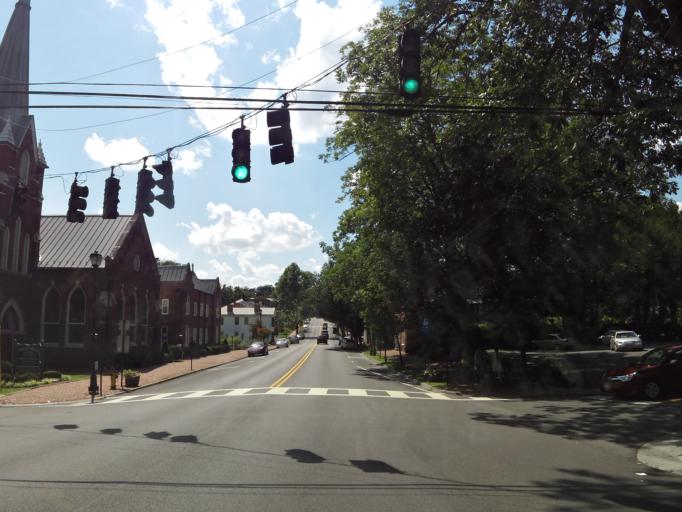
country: US
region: Virginia
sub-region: Washington County
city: Abingdon
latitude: 36.7117
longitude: -81.9717
